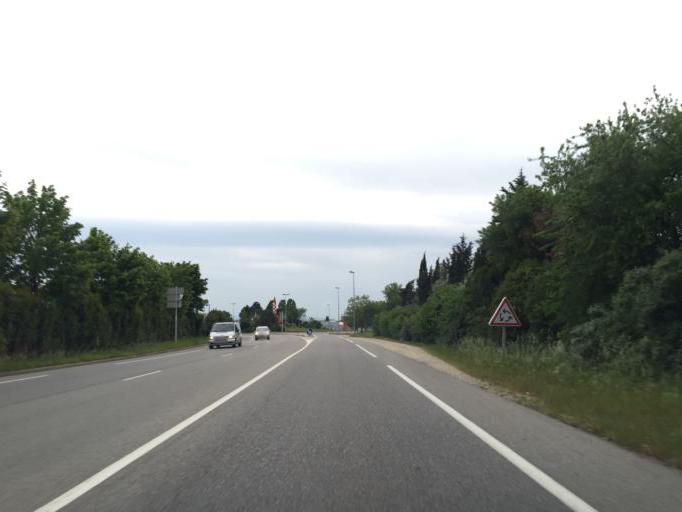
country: FR
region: Rhone-Alpes
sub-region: Departement de la Drome
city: Chabeuil
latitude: 44.9043
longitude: 5.0095
